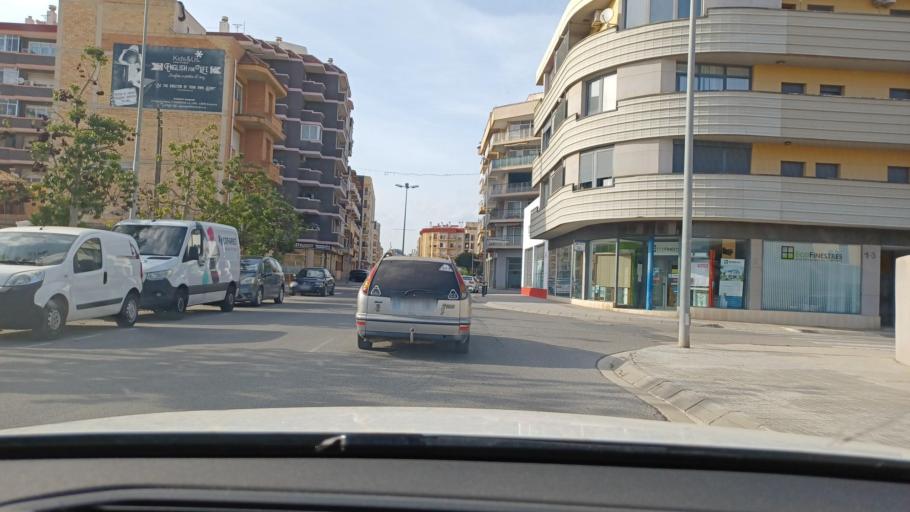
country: ES
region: Catalonia
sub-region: Provincia de Tarragona
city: Amposta
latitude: 40.7018
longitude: 0.5798
